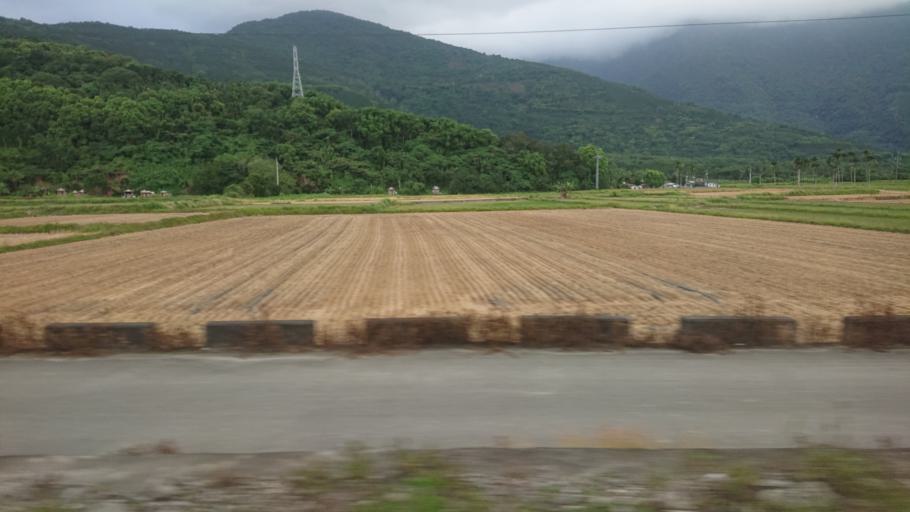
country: TW
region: Taiwan
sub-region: Hualien
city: Hualian
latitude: 23.7345
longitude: 121.4409
